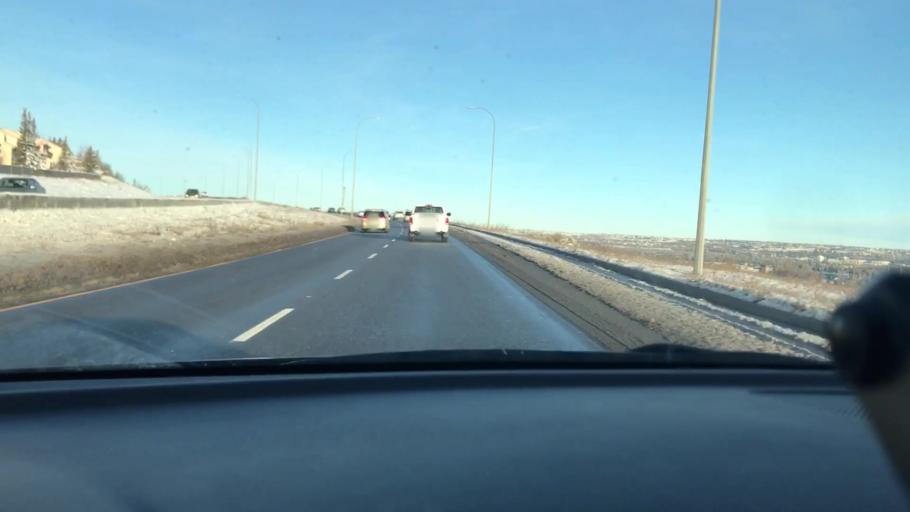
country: CA
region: Alberta
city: Calgary
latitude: 51.0617
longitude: -114.1654
